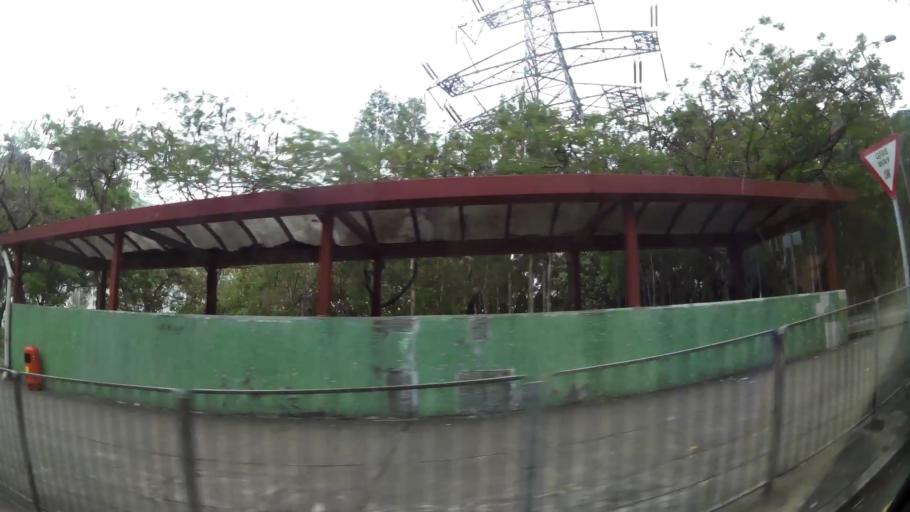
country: HK
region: Tsuen Wan
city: Tsuen Wan
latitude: 22.3803
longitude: 114.1336
